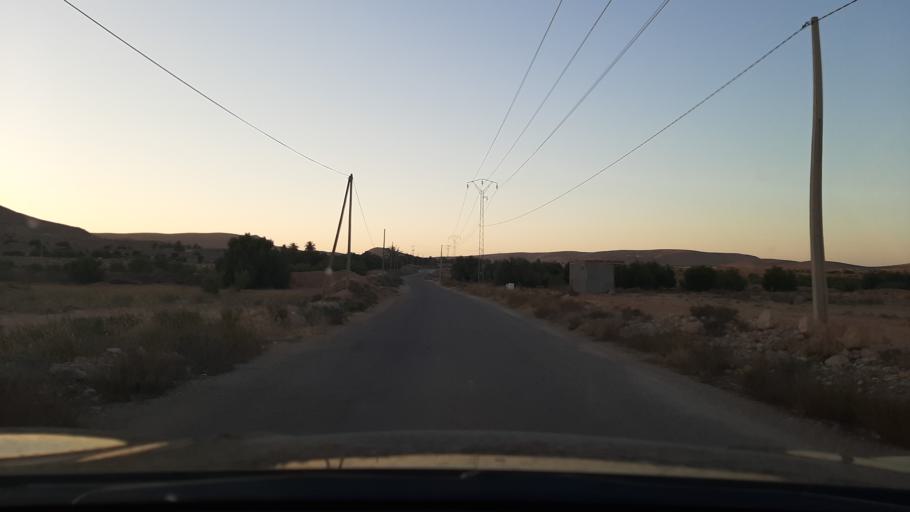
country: TN
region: Qabis
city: Matmata
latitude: 33.5513
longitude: 10.1879
